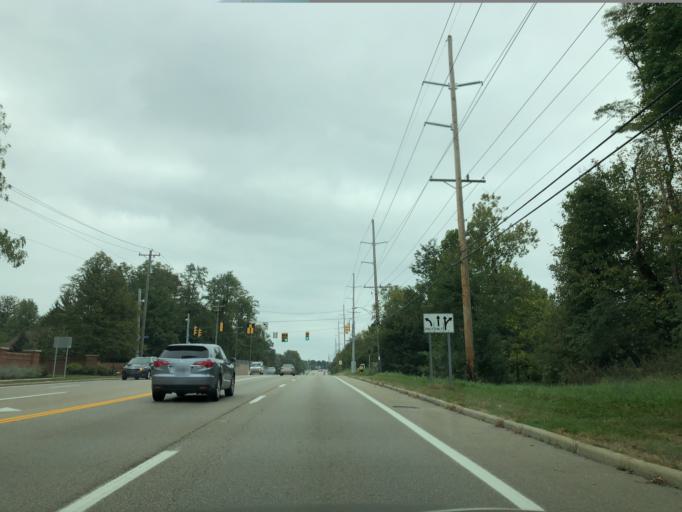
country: US
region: Ohio
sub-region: Hamilton County
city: Sixteen Mile Stand
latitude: 39.2771
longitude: -84.3226
